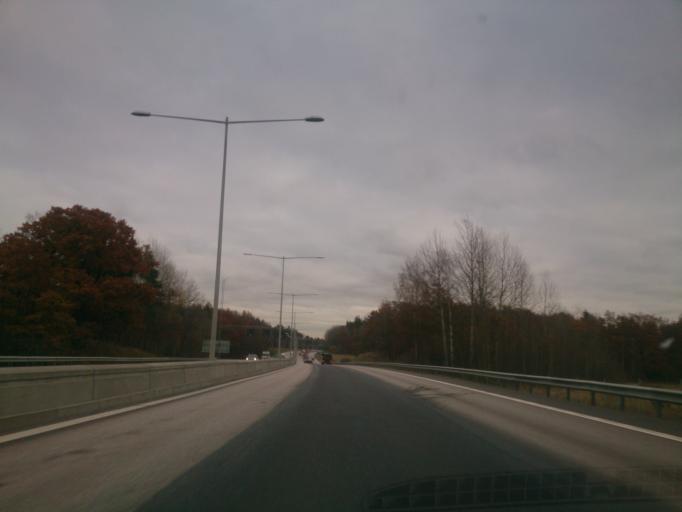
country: SE
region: Stockholm
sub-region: Salems Kommun
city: Ronninge
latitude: 59.2109
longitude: 17.7376
